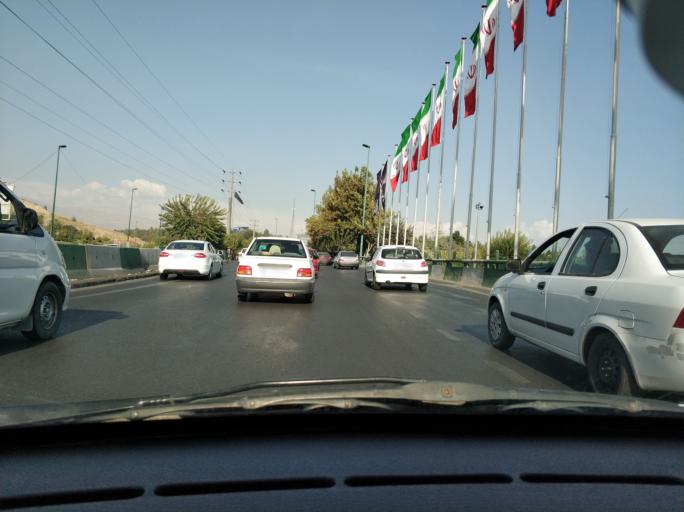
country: IR
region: Tehran
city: Tehran
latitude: 35.7409
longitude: 51.4323
